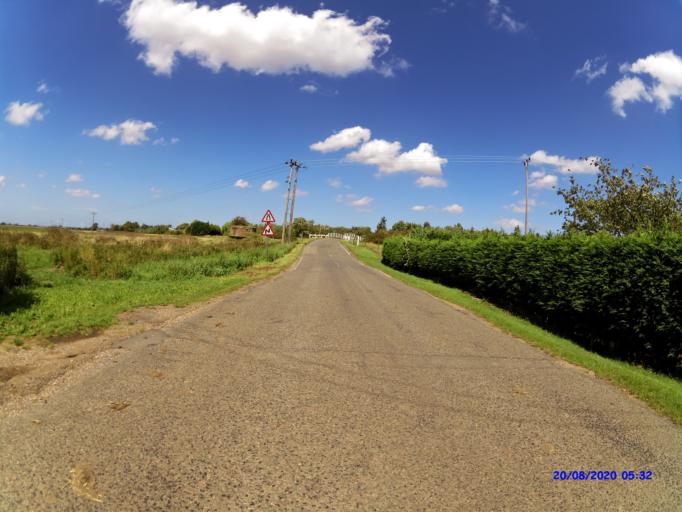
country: GB
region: England
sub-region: Cambridgeshire
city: Whittlesey
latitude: 52.5430
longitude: -0.1106
